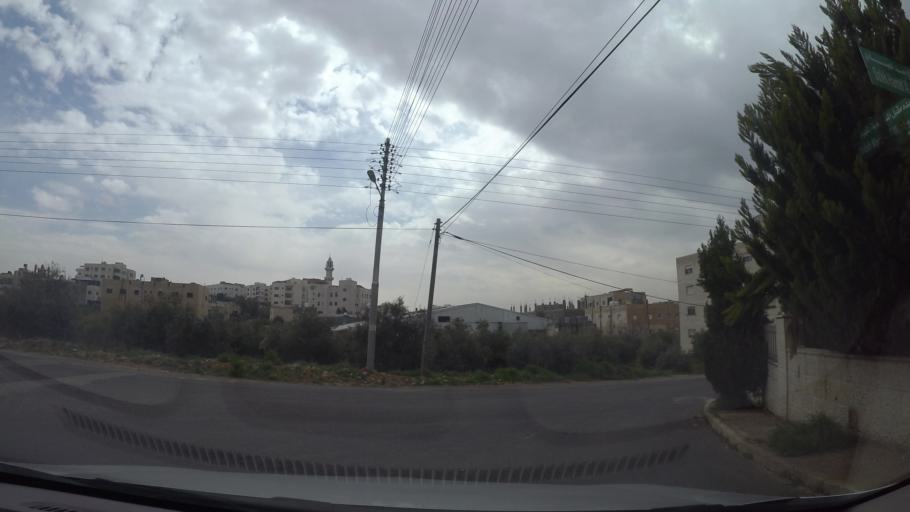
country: JO
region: Amman
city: Umm as Summaq
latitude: 31.9101
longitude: 35.8480
